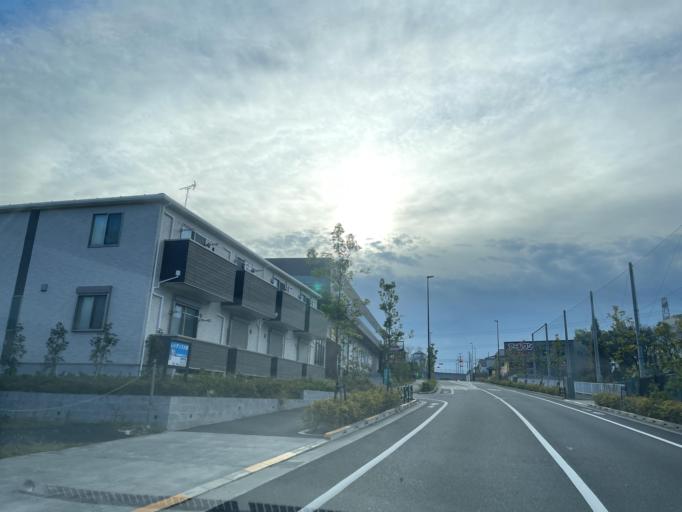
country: JP
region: Tokyo
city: Chofugaoka
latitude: 35.6171
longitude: 139.4811
